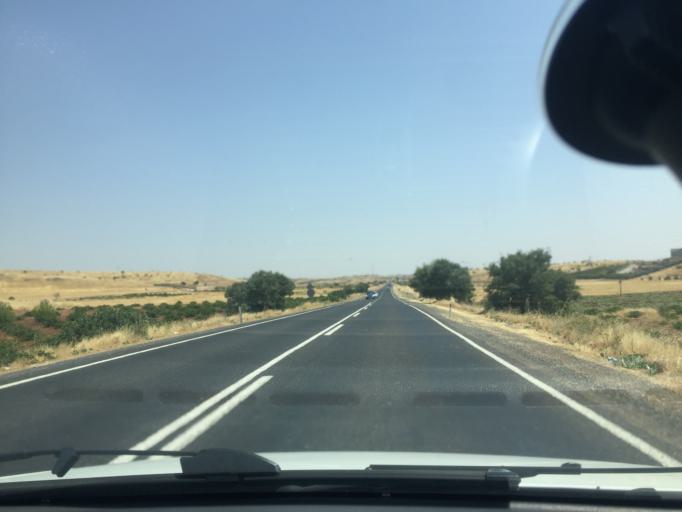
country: TR
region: Mardin
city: Kindirip
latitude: 37.4543
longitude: 41.2510
